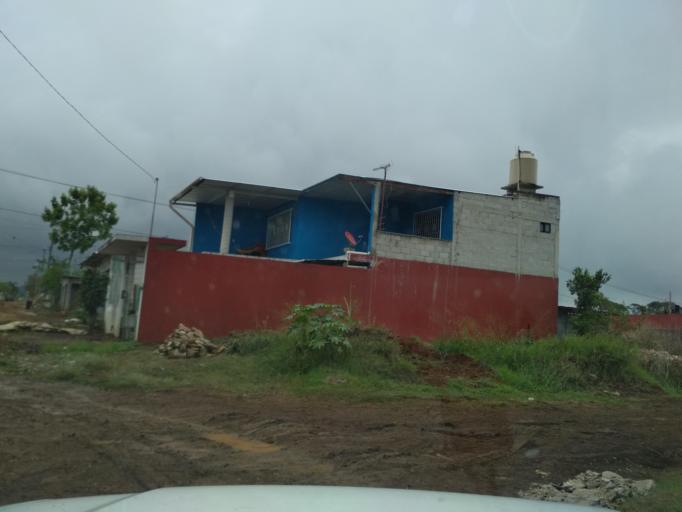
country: MX
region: Veracruz
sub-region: Cordoba
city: San Jose de Tapia
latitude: 18.8432
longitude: -96.9655
